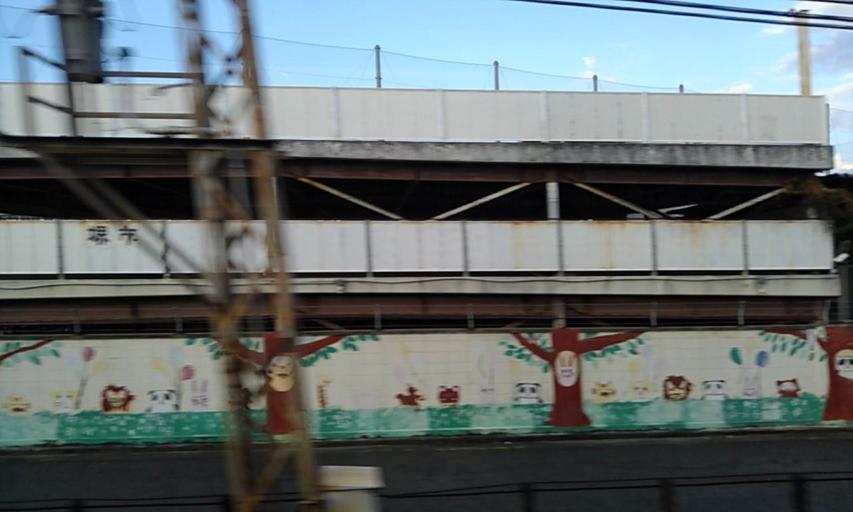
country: JP
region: Osaka
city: Sakai
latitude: 34.5621
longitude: 135.4968
